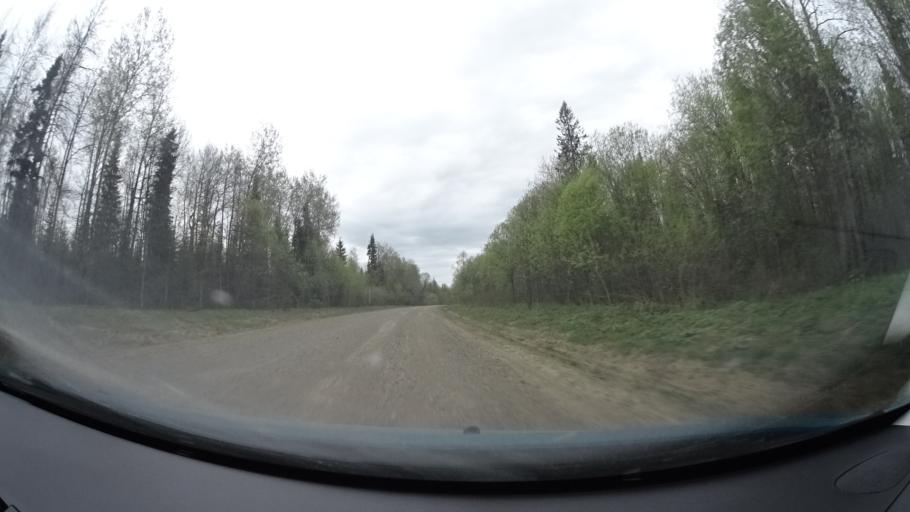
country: RU
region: Perm
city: Kuyeda
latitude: 56.5947
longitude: 55.7057
